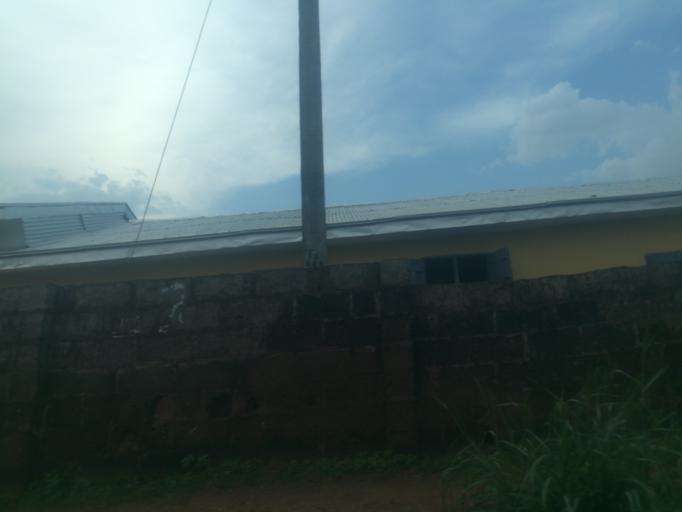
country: NG
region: Oyo
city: Ibadan
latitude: 7.3653
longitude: 3.8476
